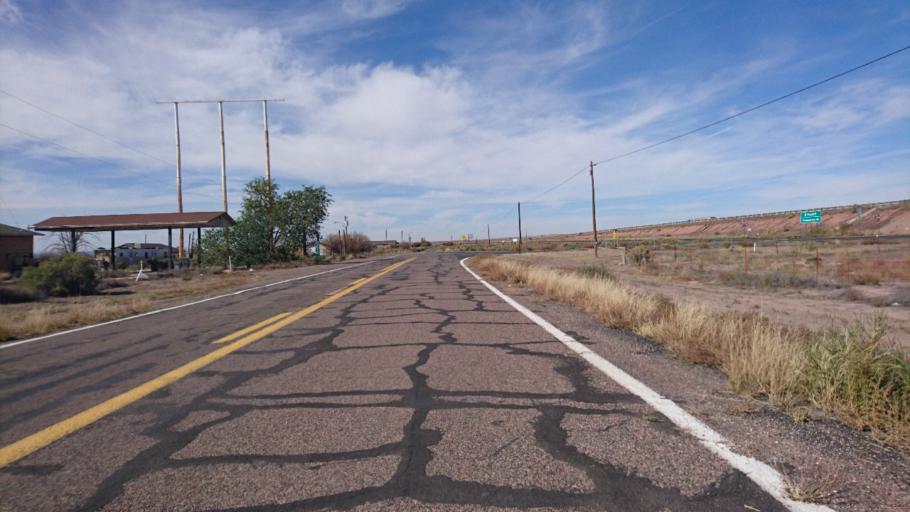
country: US
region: Arizona
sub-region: Navajo County
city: Joseph City
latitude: 34.9682
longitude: -110.4331
